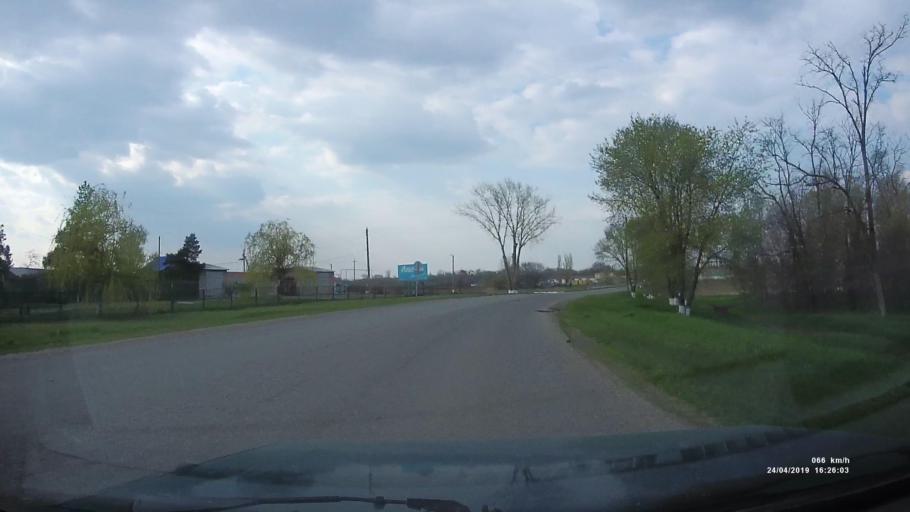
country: RU
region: Rostov
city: Orlovskiy
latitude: 46.8591
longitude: 42.0368
